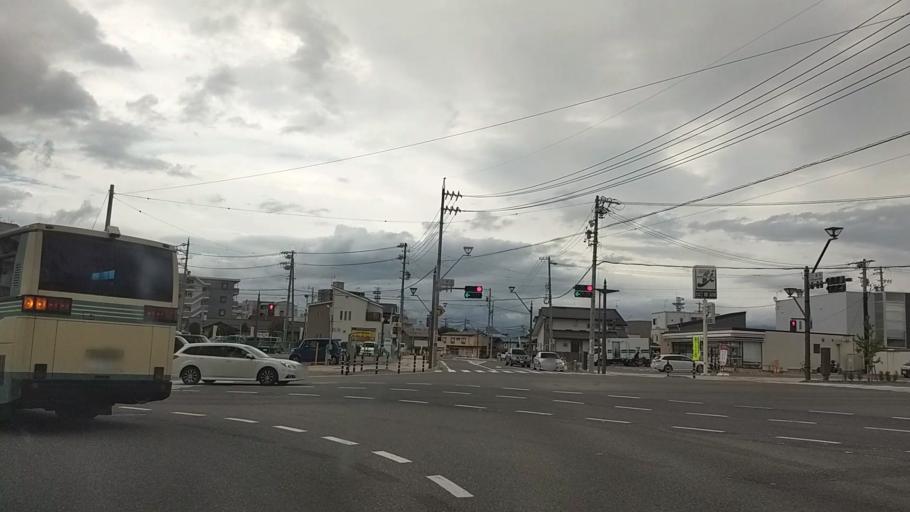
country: JP
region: Nagano
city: Nagano-shi
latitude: 36.6444
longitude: 138.1931
